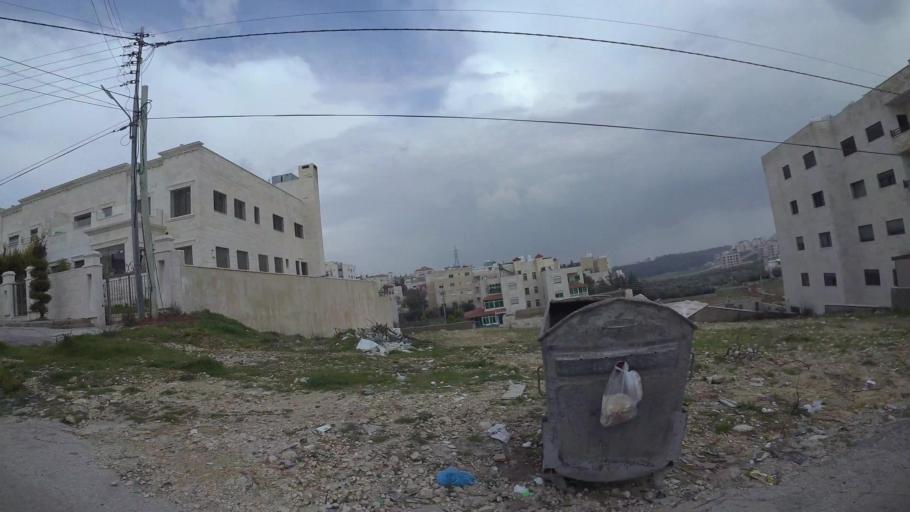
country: JO
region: Amman
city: Umm as Summaq
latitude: 31.8831
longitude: 35.8655
